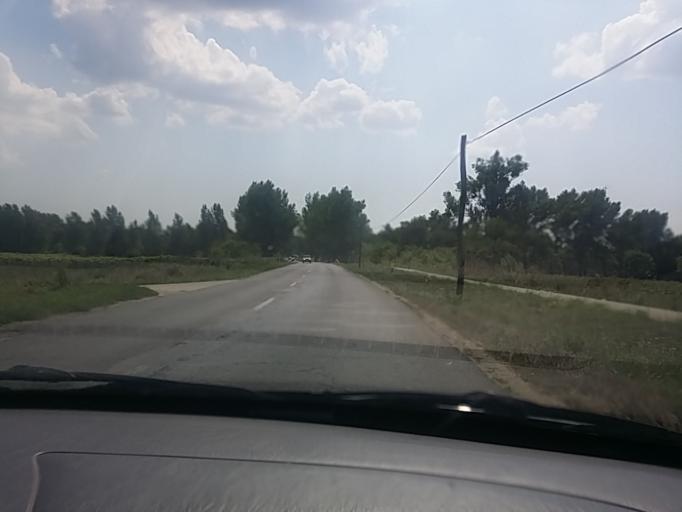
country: HU
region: Tolna
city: Dombovar
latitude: 46.3603
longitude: 18.1254
